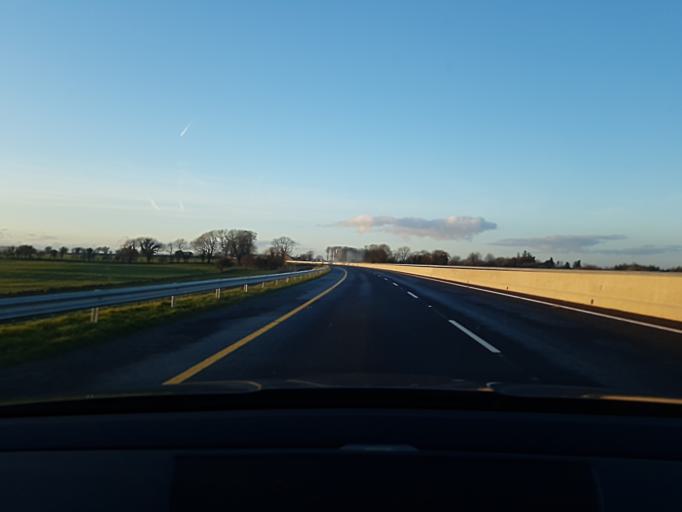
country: IE
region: Connaught
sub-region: County Galway
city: Tuam
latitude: 53.4603
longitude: -8.8499
